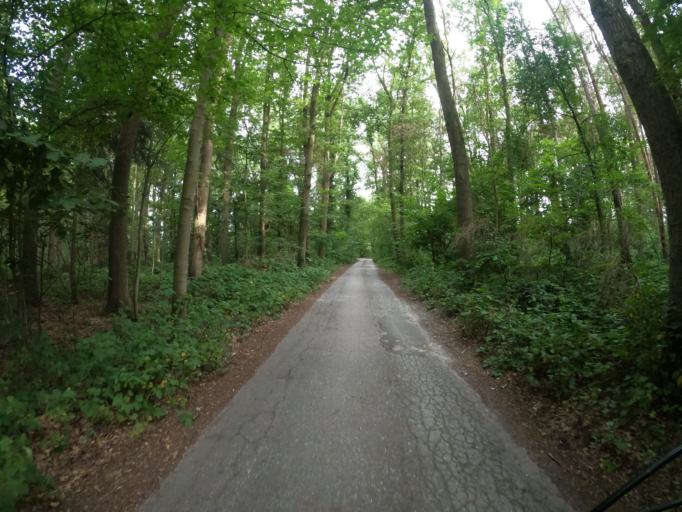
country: DE
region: North Rhine-Westphalia
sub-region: Regierungsbezirk Arnsberg
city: Lippstadt
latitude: 51.6996
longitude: 8.3227
